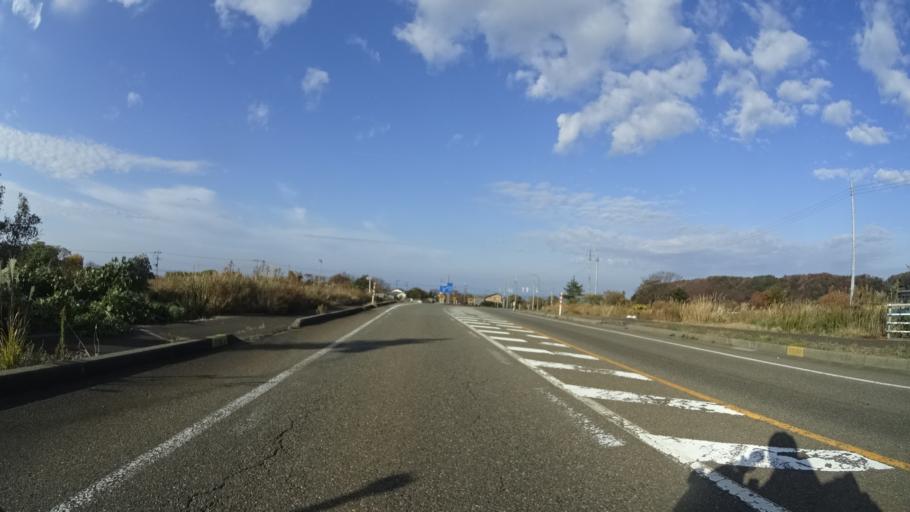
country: JP
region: Niigata
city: Kashiwazaki
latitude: 37.3277
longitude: 138.4557
